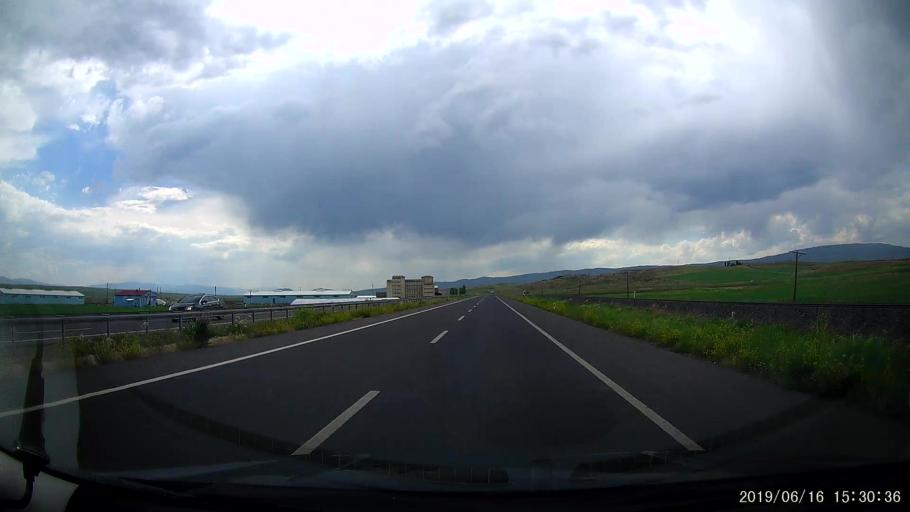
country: TR
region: Erzurum
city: Horasan
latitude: 40.0341
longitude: 42.1007
